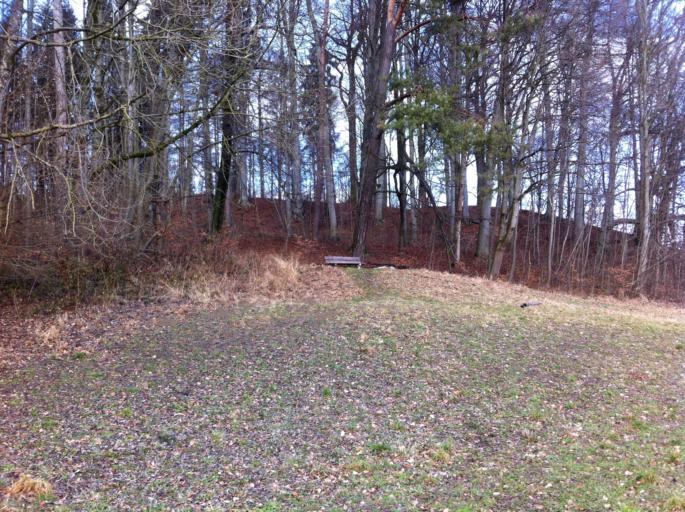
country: CH
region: Zurich
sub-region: Bezirk Zuerich
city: Zuerich (Kreis 3) / Alt-Wiedikon
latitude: 47.3533
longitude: 8.5183
